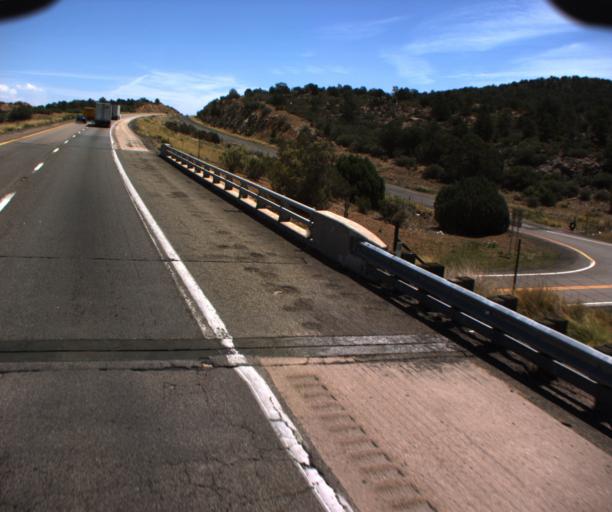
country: US
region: Arizona
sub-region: Mohave County
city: Peach Springs
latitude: 35.2049
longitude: -113.2976
